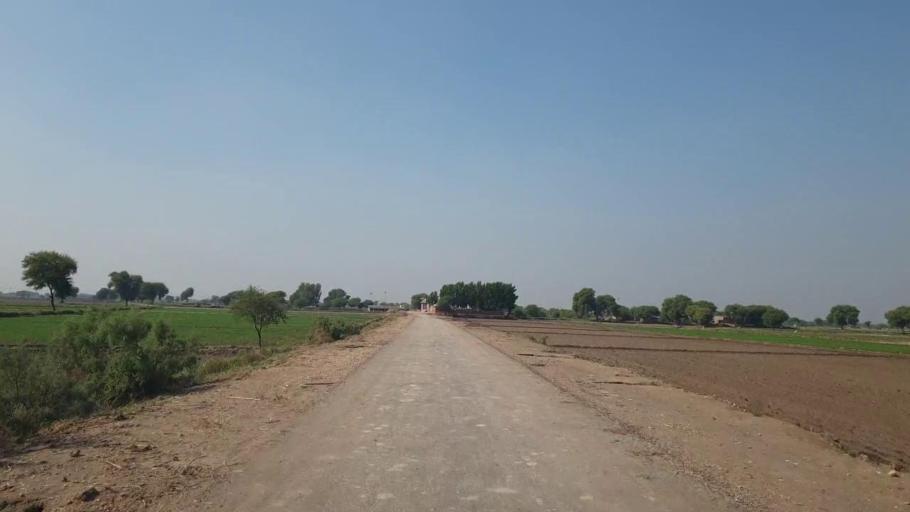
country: PK
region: Sindh
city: Sehwan
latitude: 26.4286
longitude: 67.8209
